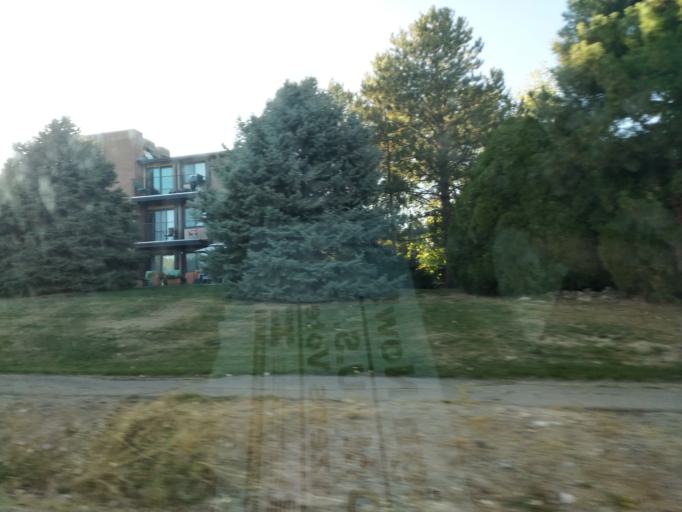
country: US
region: Colorado
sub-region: Mesa County
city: Redlands
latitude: 39.0594
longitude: -108.6103
